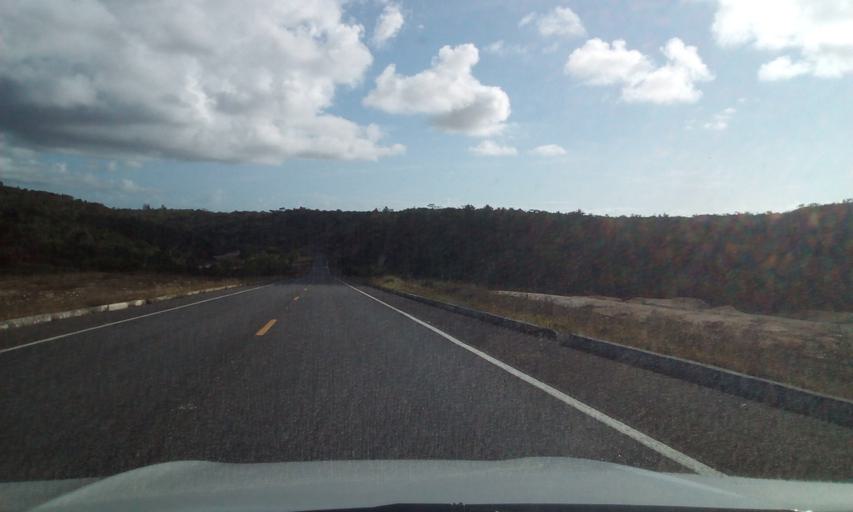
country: BR
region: Bahia
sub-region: Conde
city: Conde
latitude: -12.0770
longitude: -37.7561
